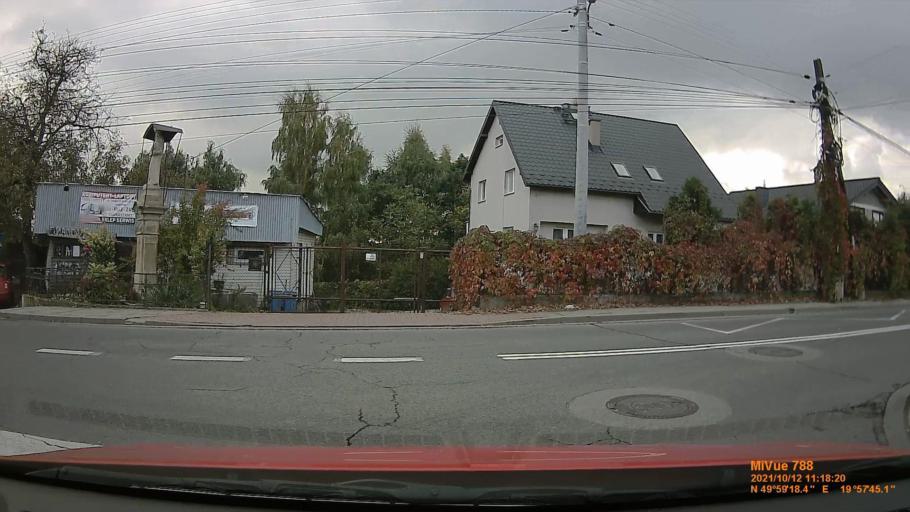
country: PL
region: Lesser Poland Voivodeship
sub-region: Powiat krakowski
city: Wrzasowice
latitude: 49.9884
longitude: 19.9625
